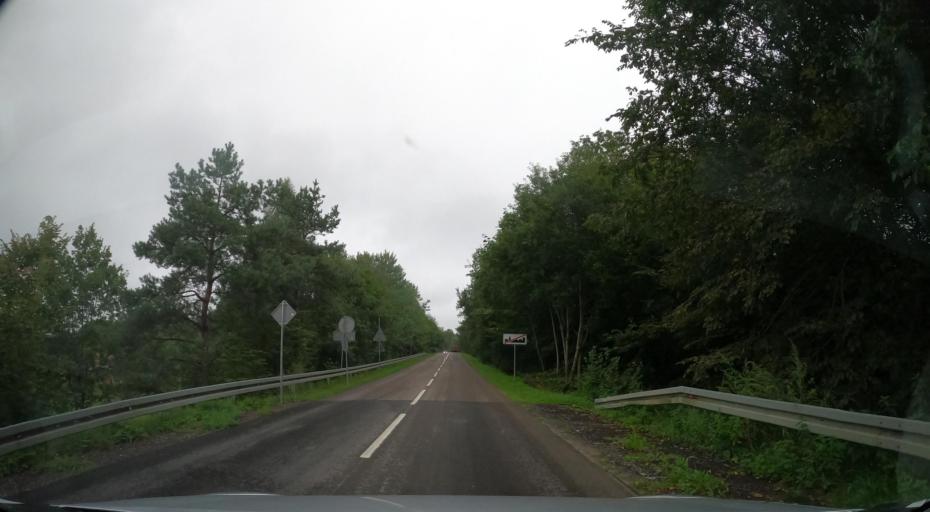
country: PL
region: Pomeranian Voivodeship
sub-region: Powiat wejherowski
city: Luzino
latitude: 54.4844
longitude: 18.1099
